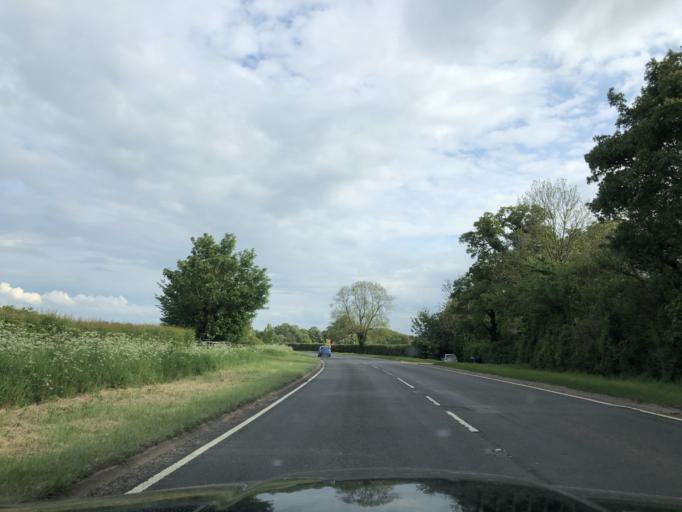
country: GB
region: England
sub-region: Warwickshire
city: Shipston on Stour
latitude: 52.1154
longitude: -1.6195
